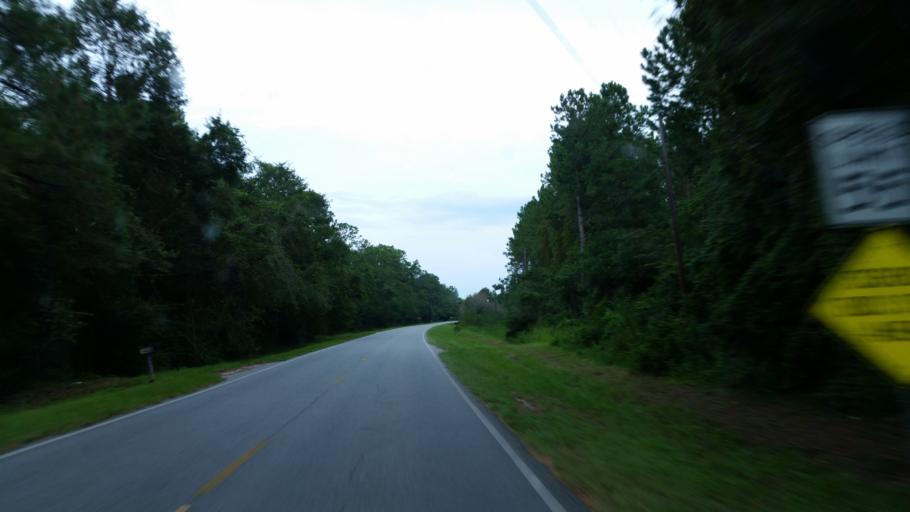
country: US
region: Georgia
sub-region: Lowndes County
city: Valdosta
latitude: 30.7536
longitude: -83.2561
